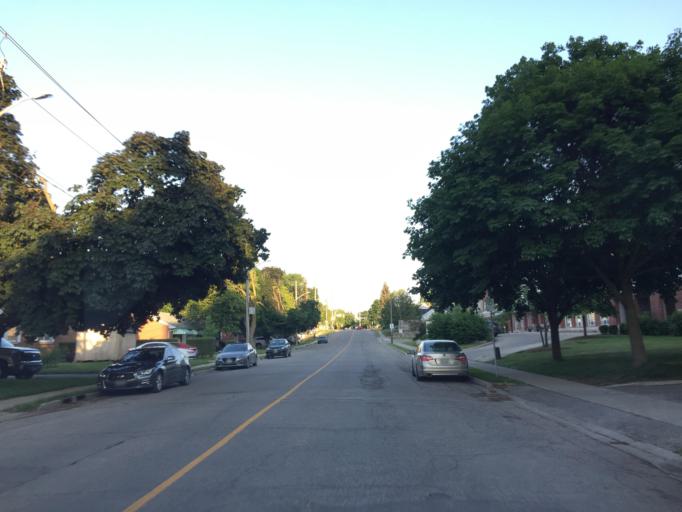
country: CA
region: Ontario
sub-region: Wellington County
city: Guelph
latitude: 43.5586
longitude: -80.2518
